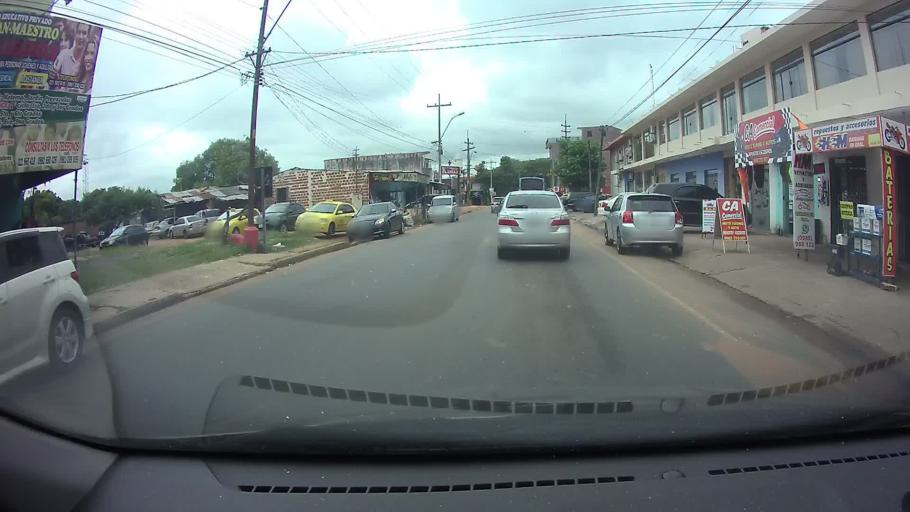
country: PY
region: Central
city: Nemby
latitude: -25.3853
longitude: -57.5484
